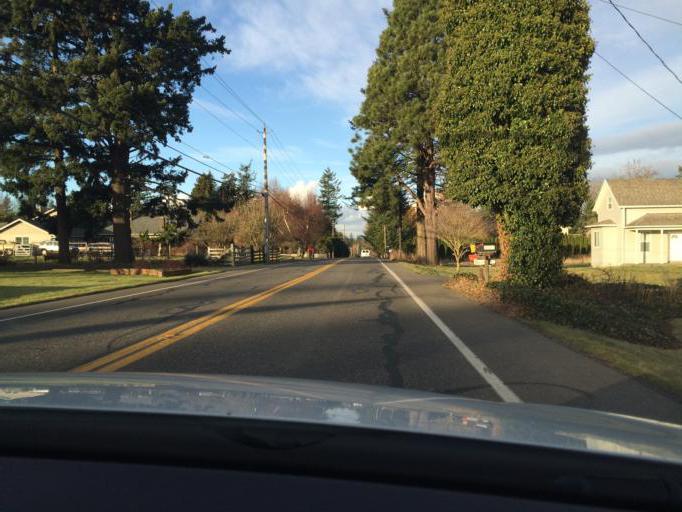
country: US
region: Washington
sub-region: Whatcom County
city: Ferndale
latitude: 48.8430
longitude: -122.5409
